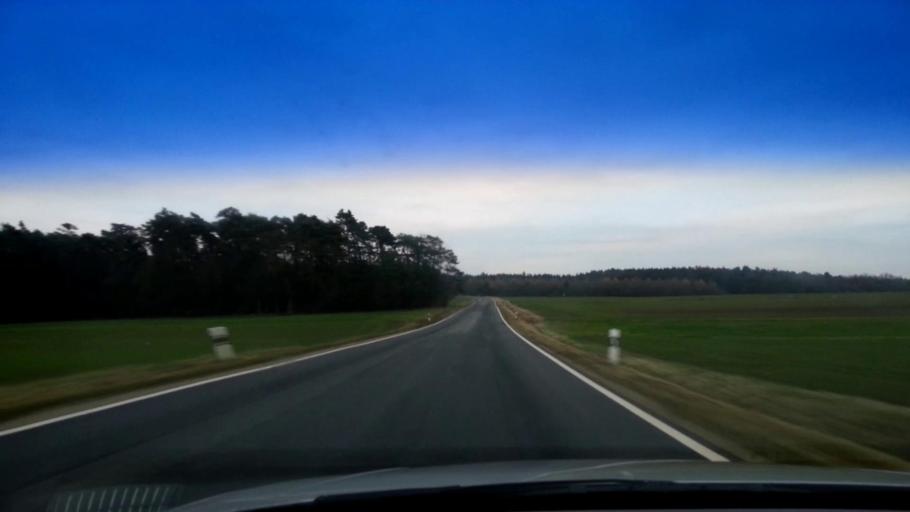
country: DE
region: Bavaria
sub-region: Regierungsbezirk Mittelfranken
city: Muhlhausen
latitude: 49.8000
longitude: 10.7837
